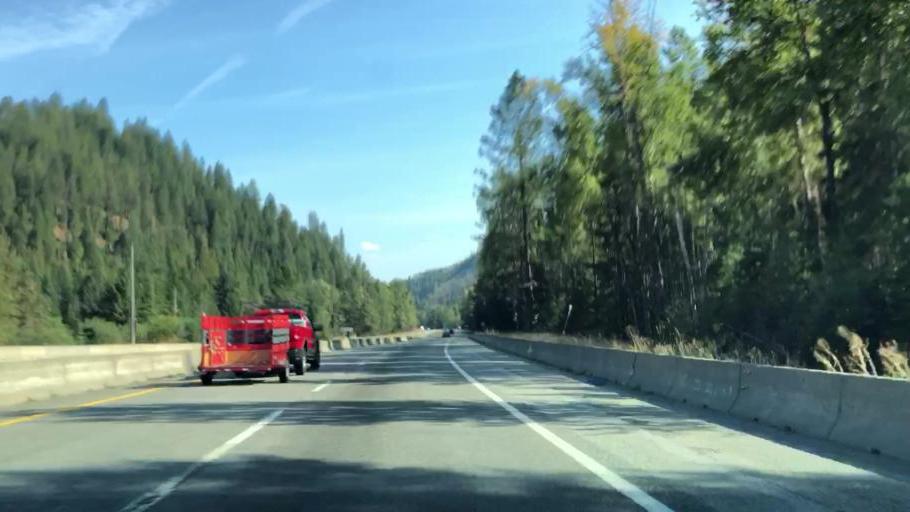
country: US
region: Idaho
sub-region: Shoshone County
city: Pinehurst
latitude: 47.5865
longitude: -116.4766
